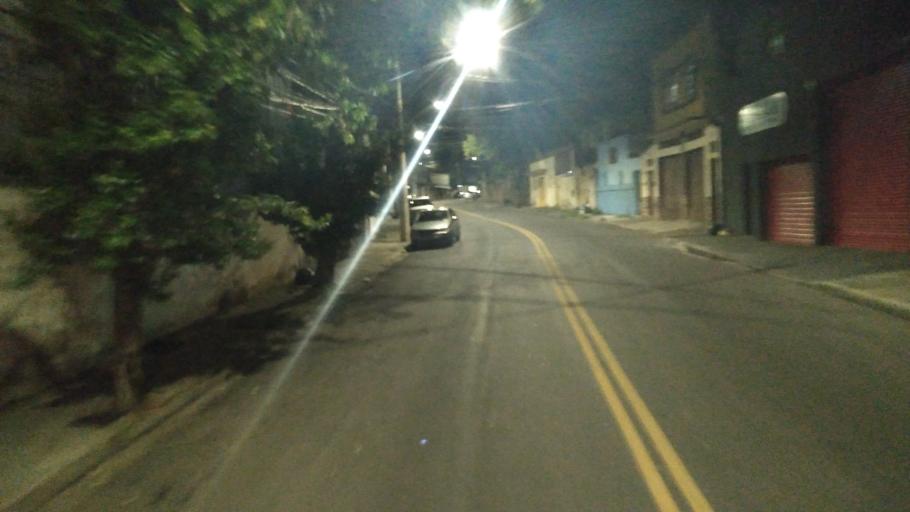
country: BR
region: Minas Gerais
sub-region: Belo Horizonte
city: Belo Horizonte
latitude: -19.9120
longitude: -43.9458
